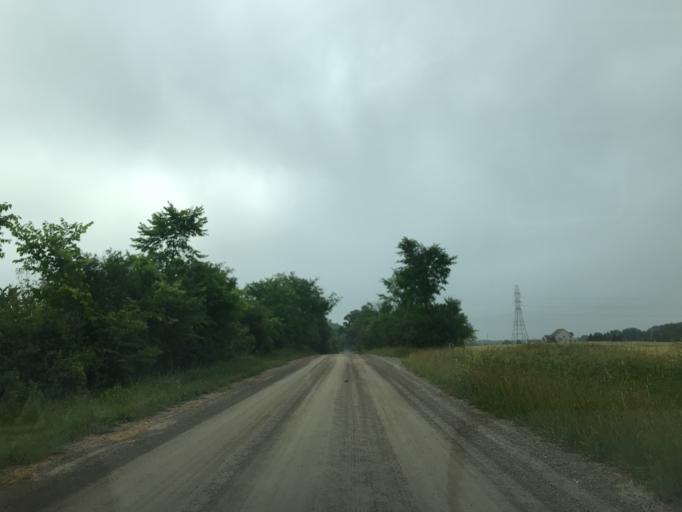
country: US
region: Michigan
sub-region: Washtenaw County
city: Ypsilanti
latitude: 42.2898
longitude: -83.6153
